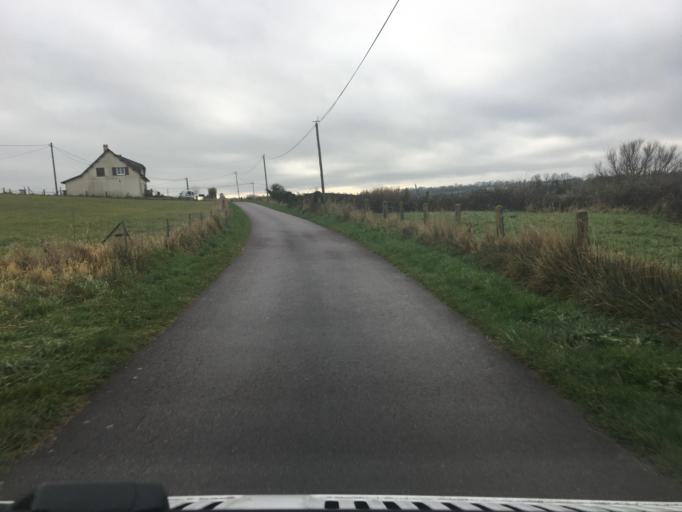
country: FR
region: Lower Normandy
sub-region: Departement du Calvados
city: Grandcamp-Maisy
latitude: 49.3910
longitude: -1.0197
